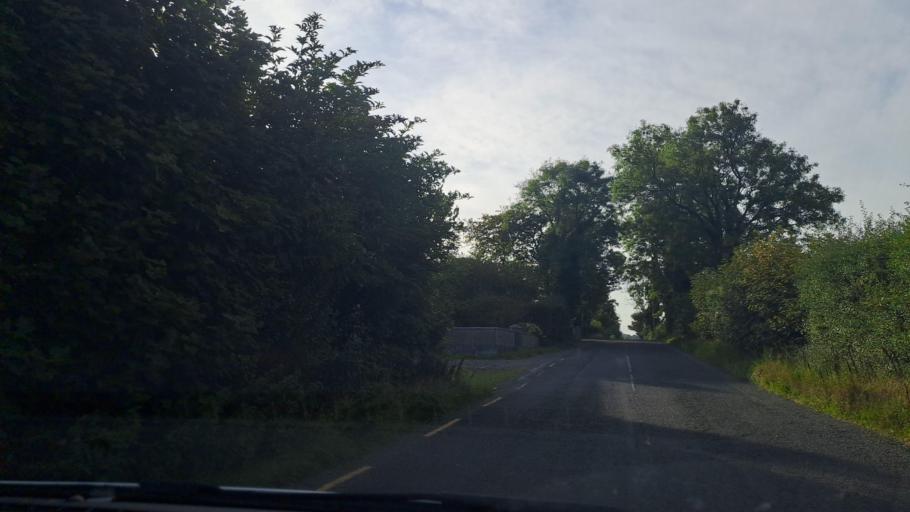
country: IE
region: Ulster
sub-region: An Cabhan
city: Kingscourt
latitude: 53.9309
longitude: -6.8171
